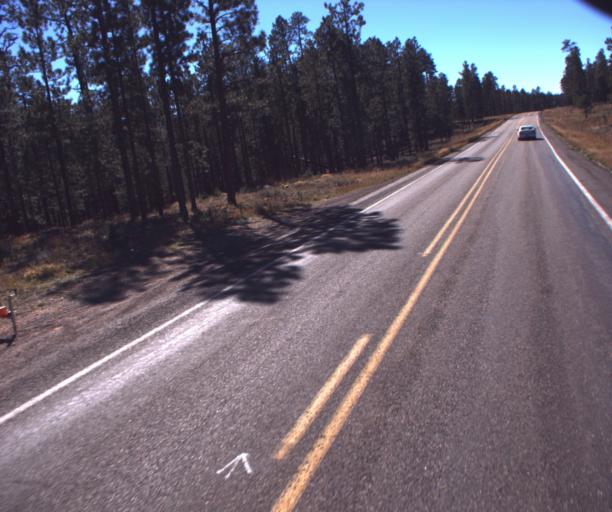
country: US
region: Arizona
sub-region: Coconino County
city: Fredonia
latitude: 36.7244
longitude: -112.2131
